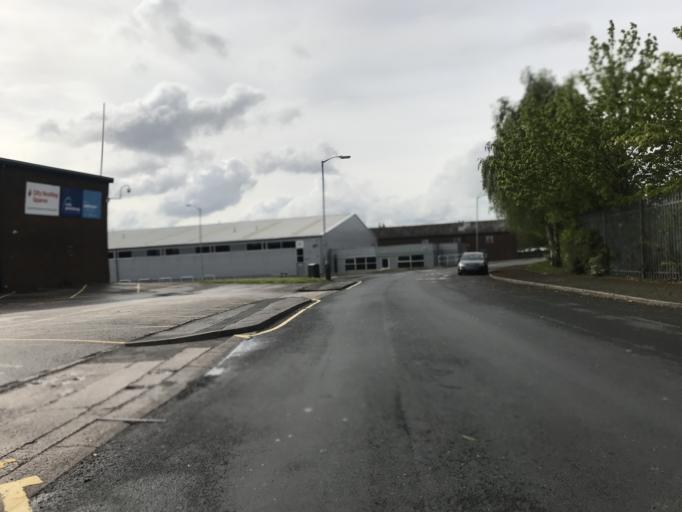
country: GB
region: England
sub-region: Borough of Stockport
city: Cheadle Heath
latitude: 53.4114
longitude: -2.1757
